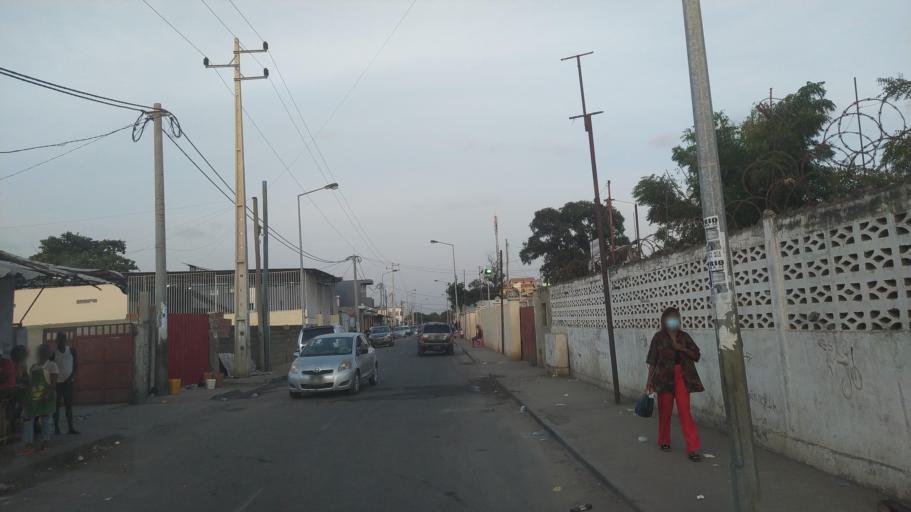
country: AO
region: Luanda
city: Luanda
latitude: -8.8885
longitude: 13.1856
